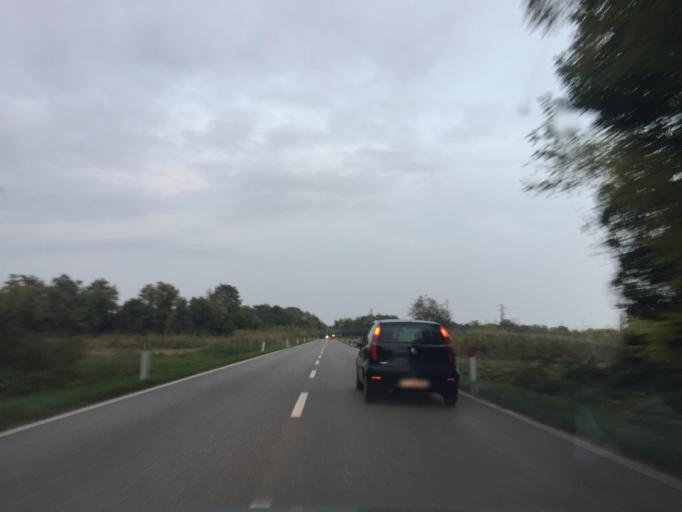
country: IT
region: Friuli Venezia Giulia
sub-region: Provincia di Pordenone
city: Fanna
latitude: 46.1713
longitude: 12.7466
